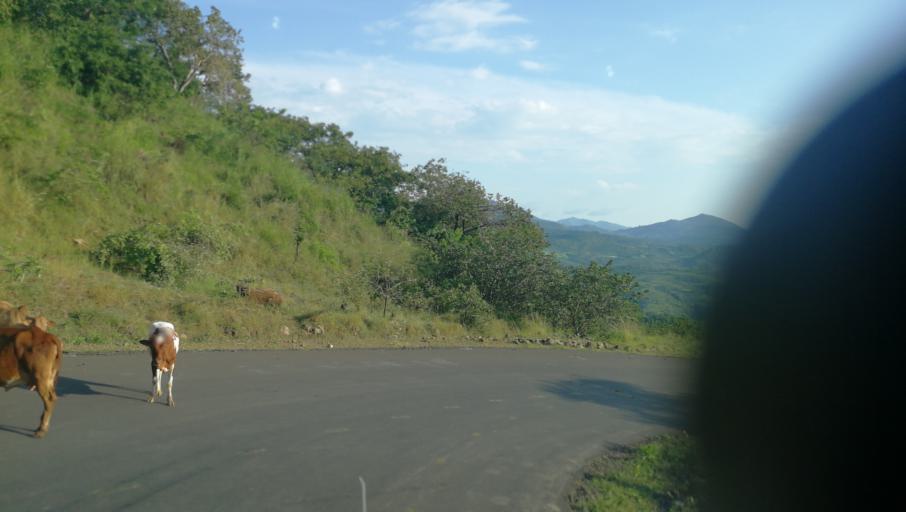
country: ET
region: Southern Nations, Nationalities, and People's Region
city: Areka
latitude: 6.8285
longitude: 37.3098
